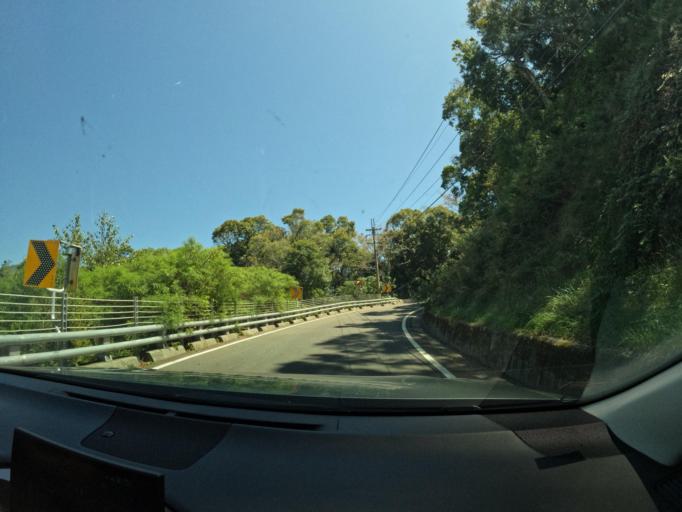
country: TW
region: Taiwan
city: Yujing
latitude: 23.2879
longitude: 120.8988
